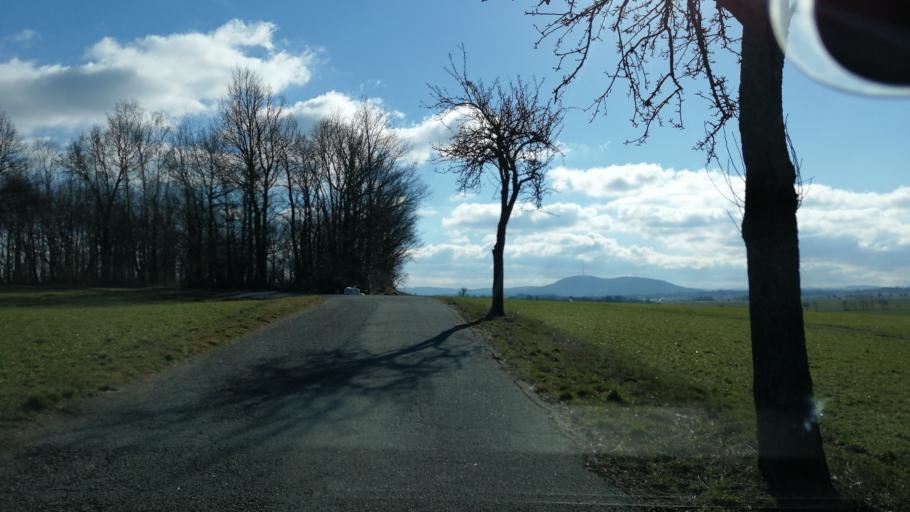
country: DE
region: Saxony
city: Weissenberg
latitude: 51.1607
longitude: 14.7207
